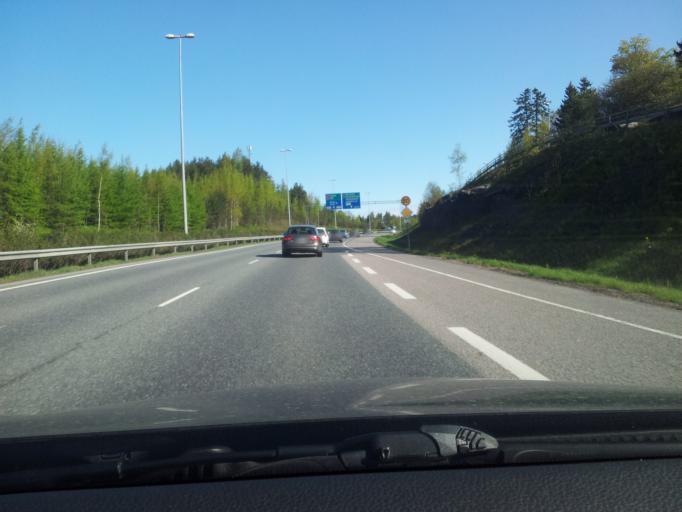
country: FI
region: Uusimaa
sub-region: Helsinki
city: Kauniainen
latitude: 60.1939
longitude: 24.7438
